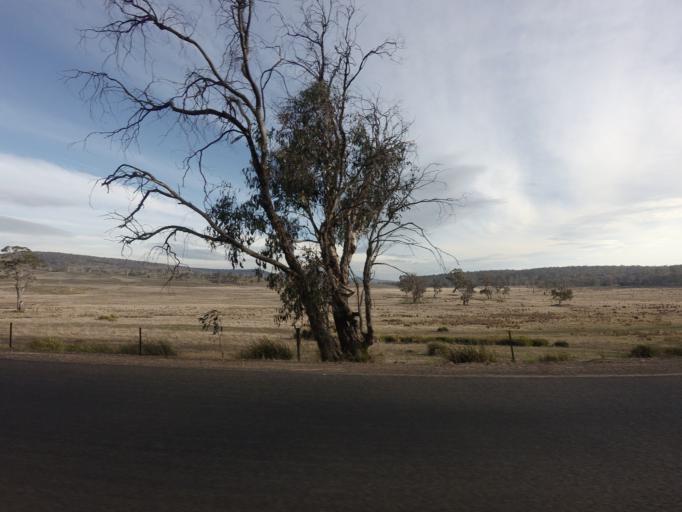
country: AU
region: Tasmania
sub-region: Brighton
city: Bridgewater
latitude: -42.3942
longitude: 147.0481
